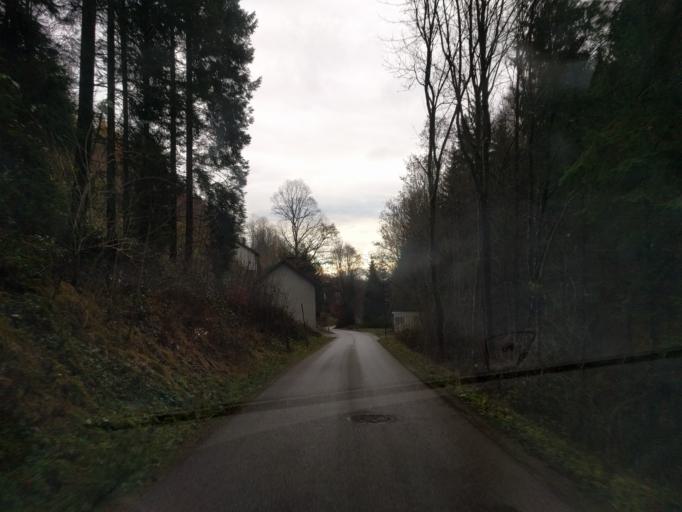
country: AT
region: Upper Austria
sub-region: Politischer Bezirk Urfahr-Umgebung
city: Kirchschlag bei Linz
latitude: 48.4095
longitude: 14.2960
